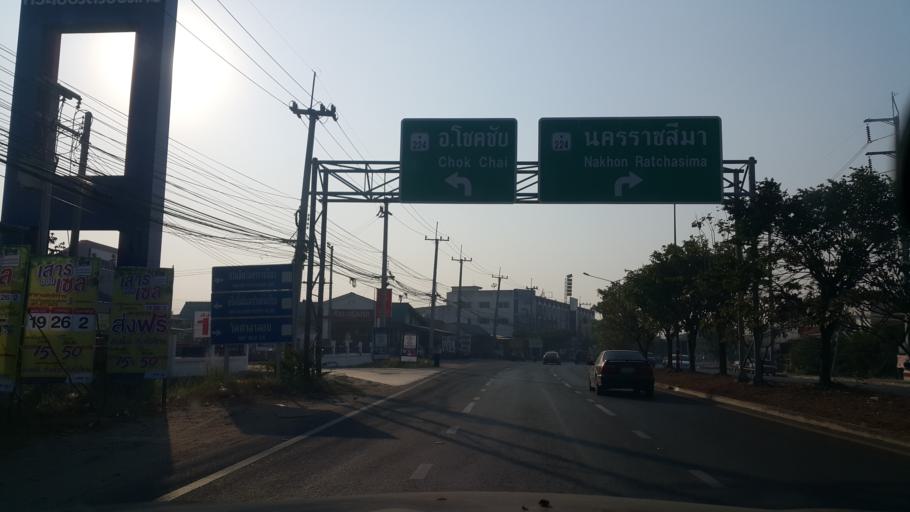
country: TH
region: Nakhon Ratchasima
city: Nakhon Ratchasima
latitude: 14.9561
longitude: 102.1231
